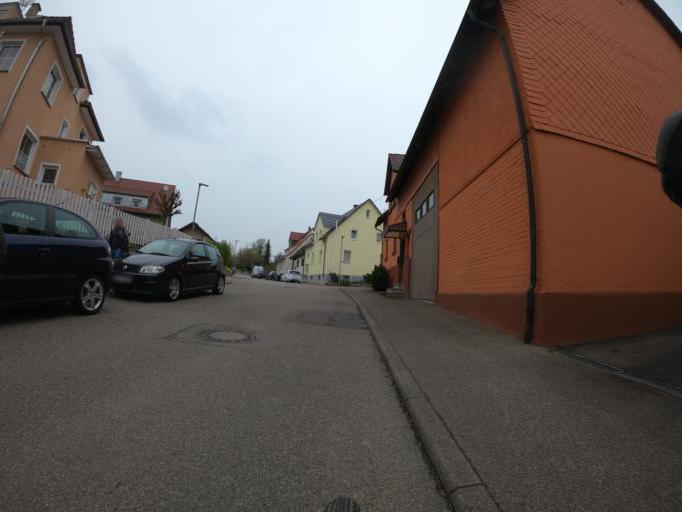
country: DE
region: Baden-Wuerttemberg
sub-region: Karlsruhe Region
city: Illingen
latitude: 48.9583
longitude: 8.9214
